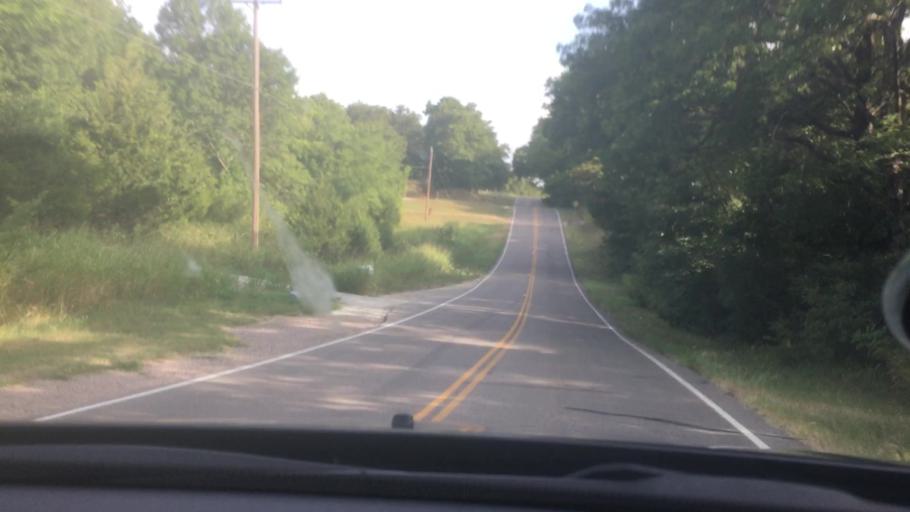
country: US
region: Oklahoma
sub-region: Pontotoc County
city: Ada
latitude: 34.7336
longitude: -96.6703
